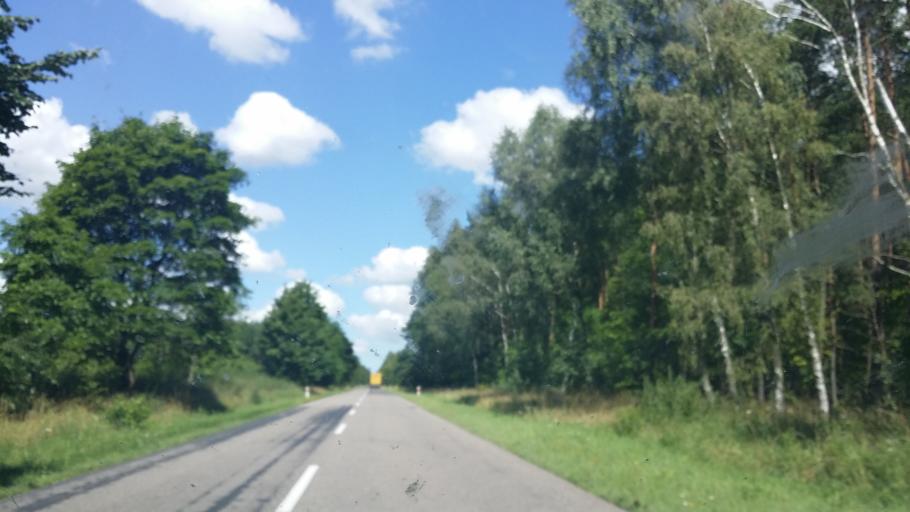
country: PL
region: West Pomeranian Voivodeship
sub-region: Powiat swidwinski
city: Slawoborze
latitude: 53.9262
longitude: 15.6824
